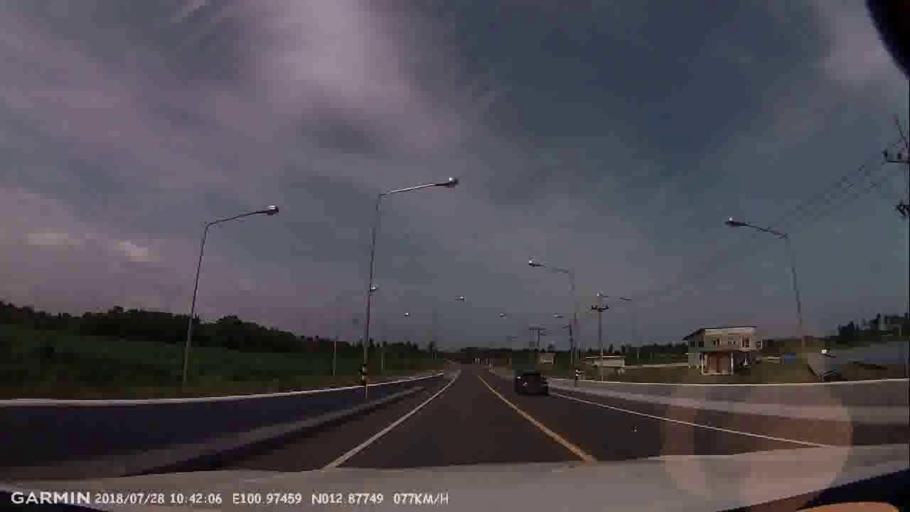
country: TH
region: Chon Buri
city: Phatthaya
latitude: 12.8774
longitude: 100.9745
